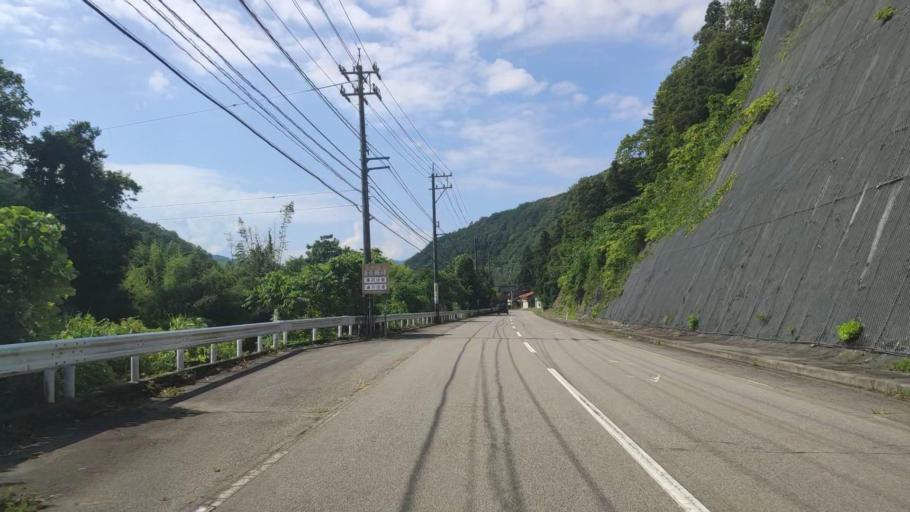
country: JP
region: Ishikawa
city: Komatsu
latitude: 36.3539
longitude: 136.5044
